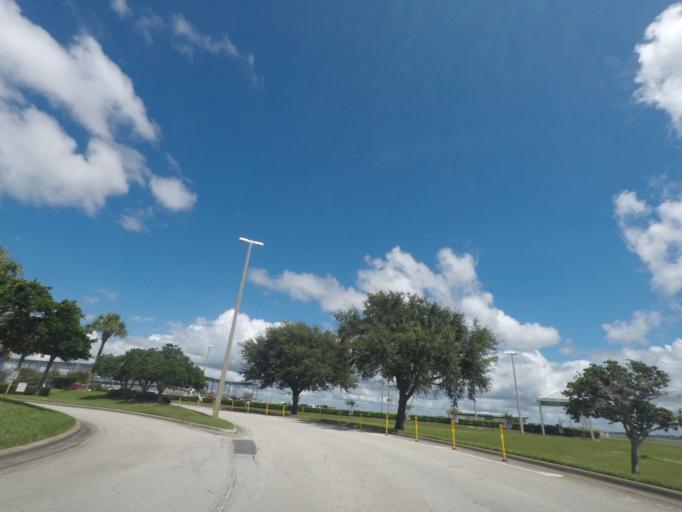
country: US
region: Florida
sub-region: Seminole County
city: Midway
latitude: 28.7747
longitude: -81.2400
